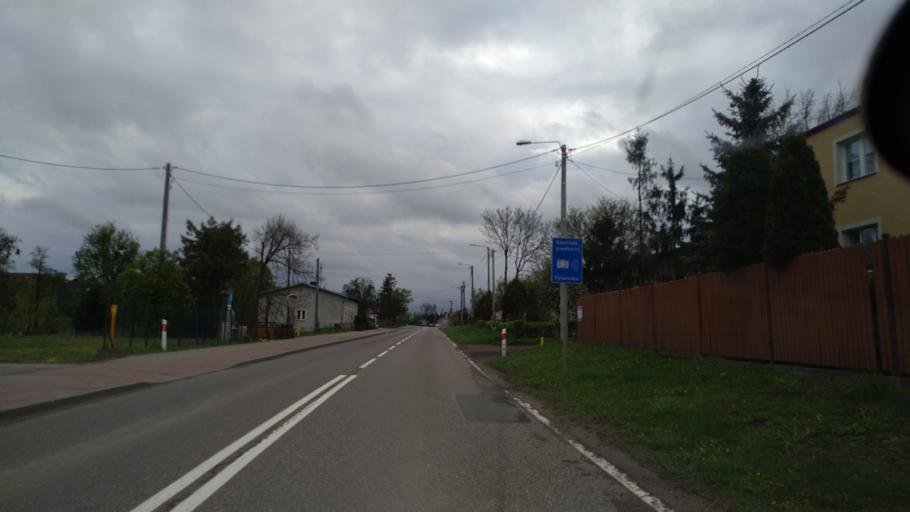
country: PL
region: Pomeranian Voivodeship
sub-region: Powiat kwidzynski
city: Kwidzyn
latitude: 53.7601
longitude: 18.9439
